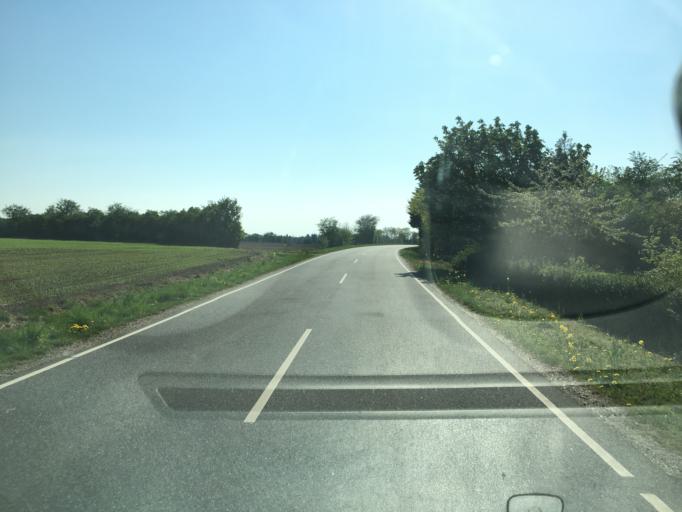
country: DK
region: South Denmark
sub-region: Haderslev Kommune
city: Vojens
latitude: 55.2955
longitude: 9.2475
